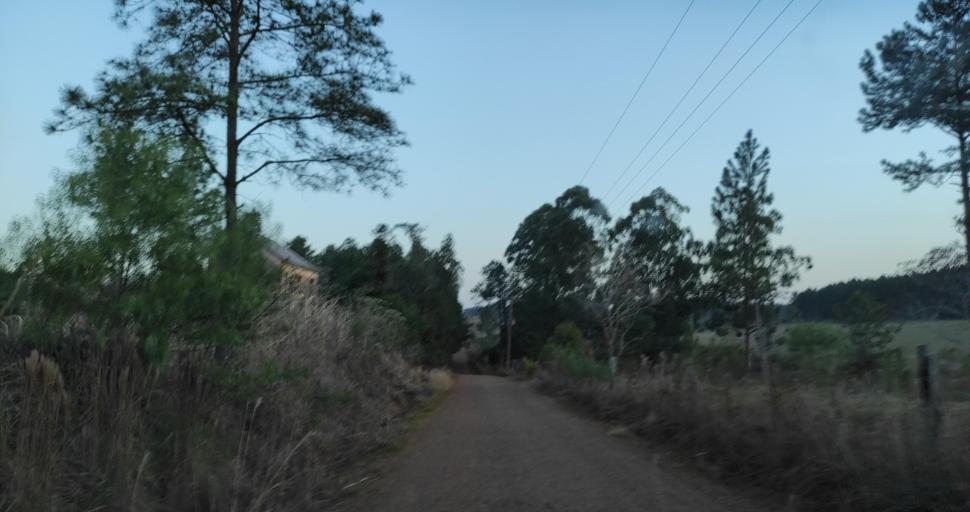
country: AR
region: Misiones
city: Capiovi
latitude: -26.8954
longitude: -55.0495
